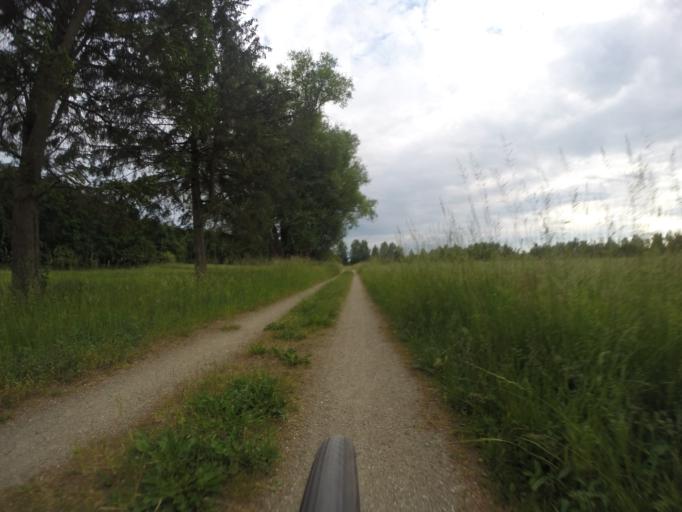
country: DK
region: Capital Region
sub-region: Ballerup Kommune
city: Ballerup
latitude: 55.7018
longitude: 12.3476
